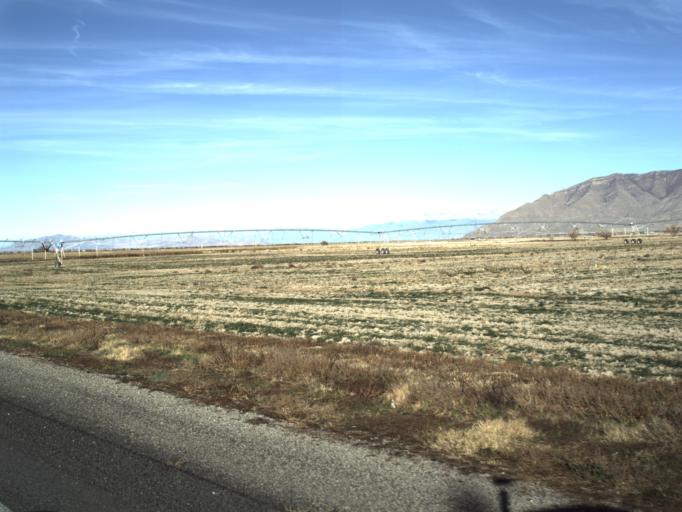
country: US
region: Utah
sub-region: Tooele County
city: Erda
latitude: 40.6118
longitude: -112.3710
